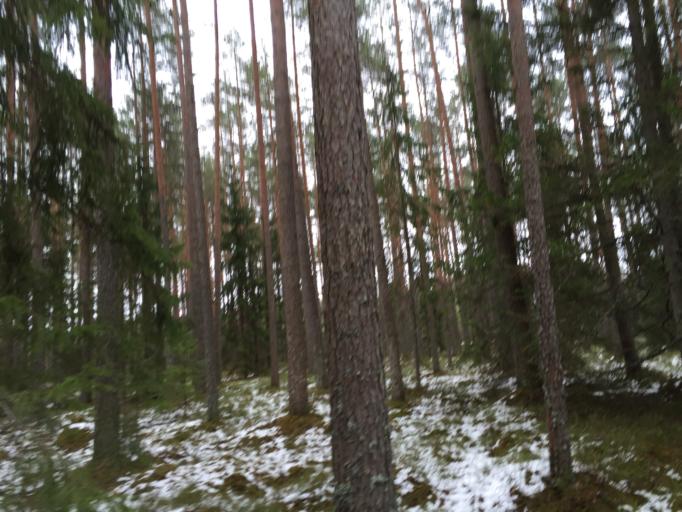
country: LV
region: Garkalne
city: Garkalne
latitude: 56.9618
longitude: 24.4783
